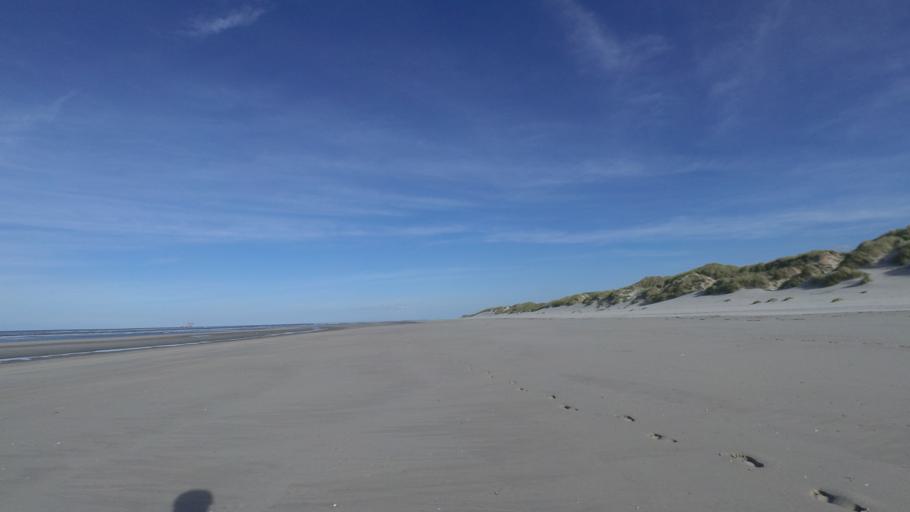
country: NL
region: Friesland
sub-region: Gemeente Dongeradeel
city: Holwerd
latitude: 53.4663
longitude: 5.8814
